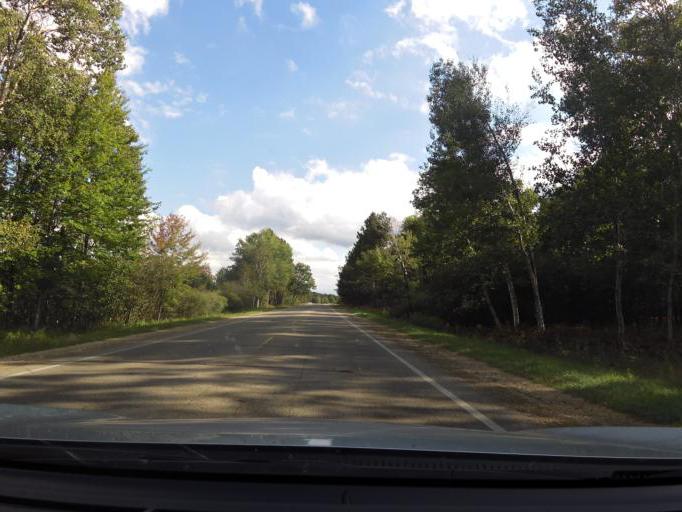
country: US
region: Michigan
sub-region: Roscommon County
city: Saint Helen
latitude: 44.3859
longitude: -84.4281
